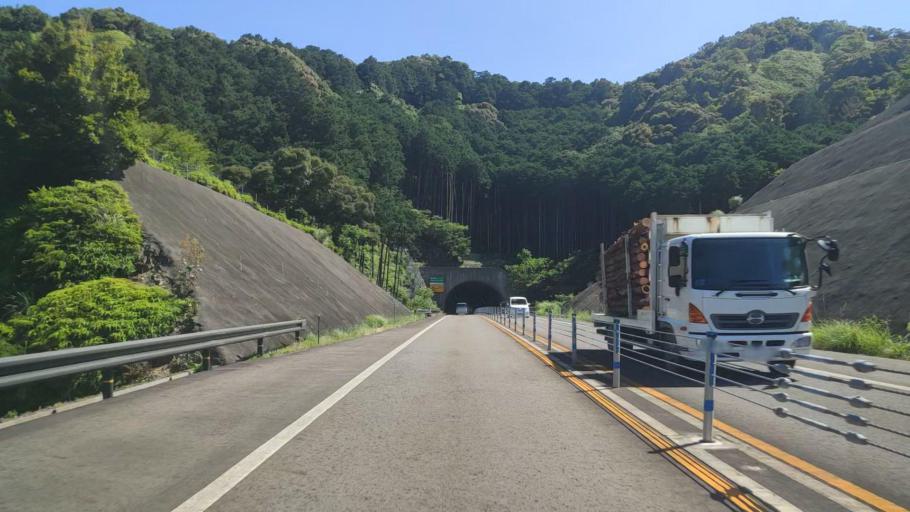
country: JP
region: Wakayama
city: Shingu
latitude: 33.6267
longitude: 135.9212
